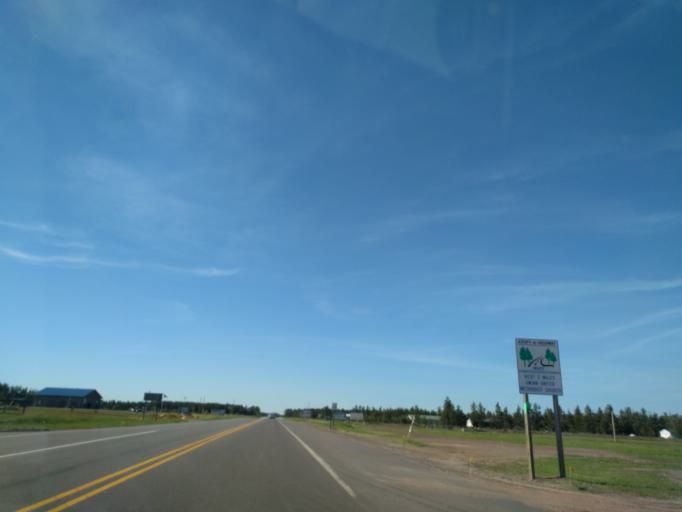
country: US
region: Michigan
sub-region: Marquette County
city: Gwinn
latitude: 46.2763
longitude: -87.4156
